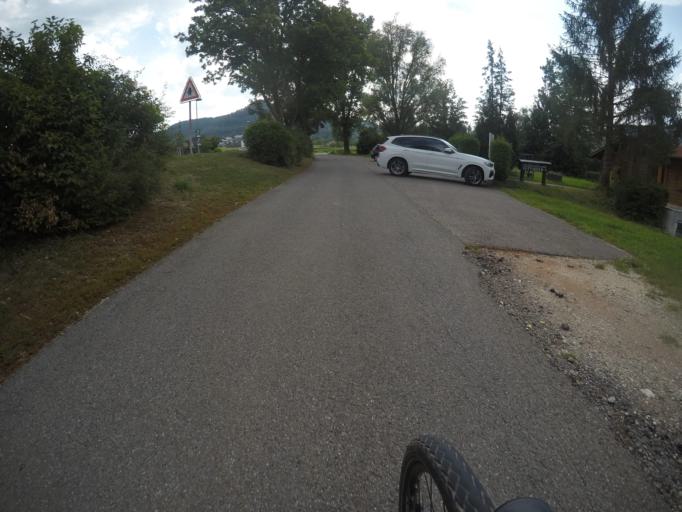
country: DE
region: Baden-Wuerttemberg
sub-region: Tuebingen Region
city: Dettingen an der Erms
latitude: 48.5230
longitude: 9.3566
